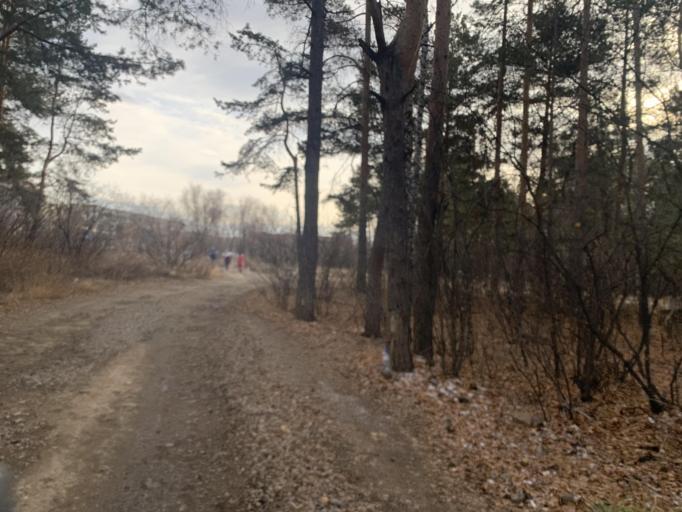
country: RU
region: Chelyabinsk
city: Roshchino
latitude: 55.1997
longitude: 61.3008
